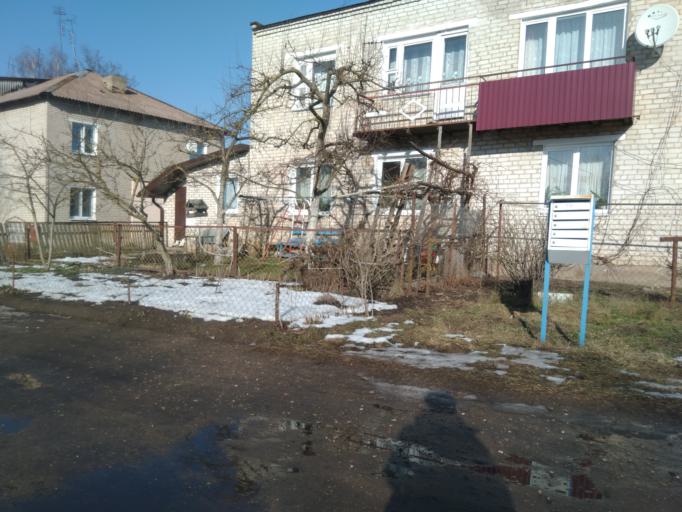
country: BY
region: Minsk
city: Nyasvizh
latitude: 53.2023
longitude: 26.6429
